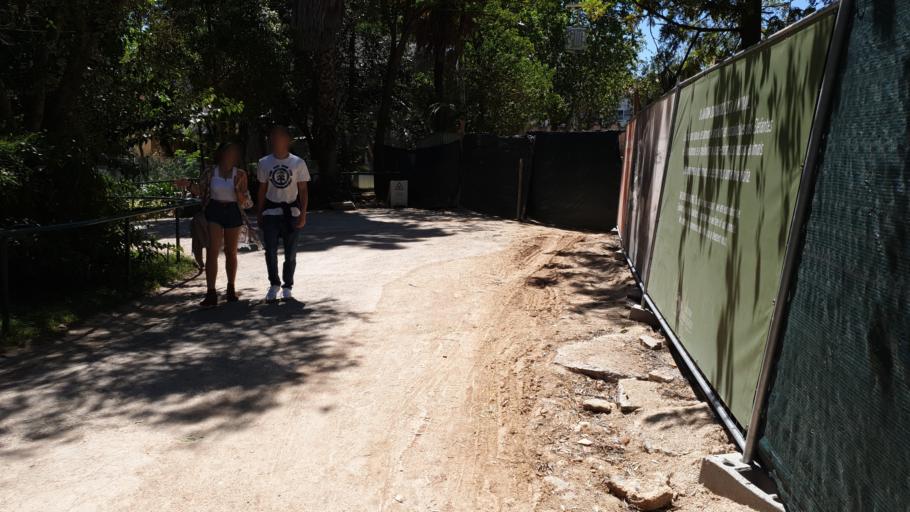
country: PT
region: Lisbon
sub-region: Odivelas
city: Pontinha
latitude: 38.7444
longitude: -9.1718
